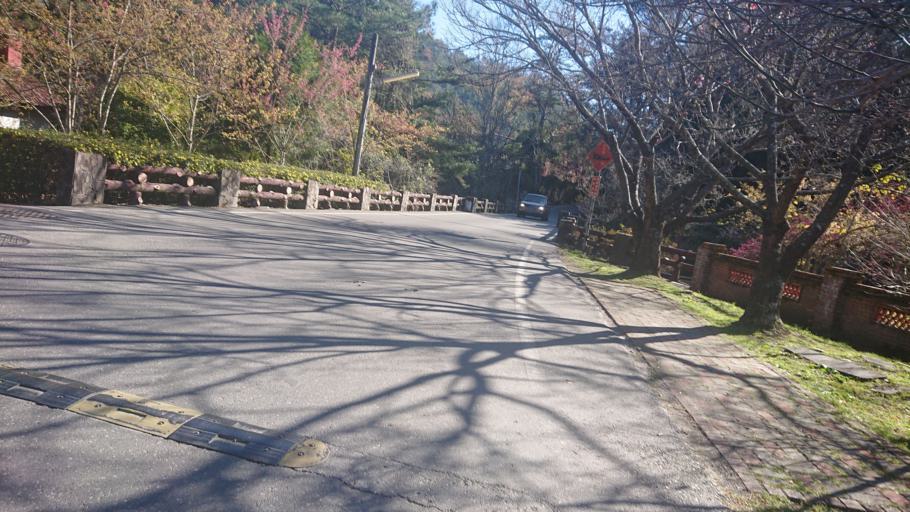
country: TW
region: Taiwan
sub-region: Hualien
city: Hualian
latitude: 24.3566
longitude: 121.3124
